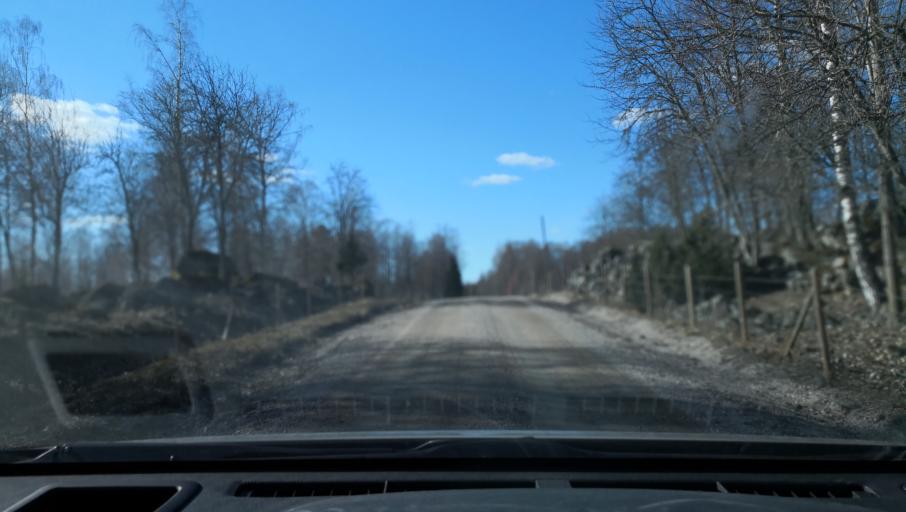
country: SE
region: Vaestmanland
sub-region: Sala Kommun
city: Sala
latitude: 60.1125
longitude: 16.6863
